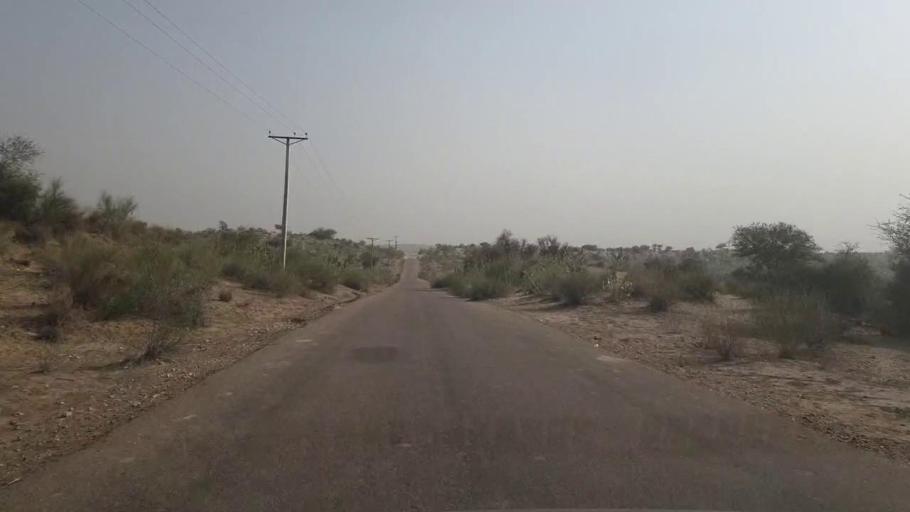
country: PK
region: Sindh
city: Chor
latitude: 25.5497
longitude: 69.9589
